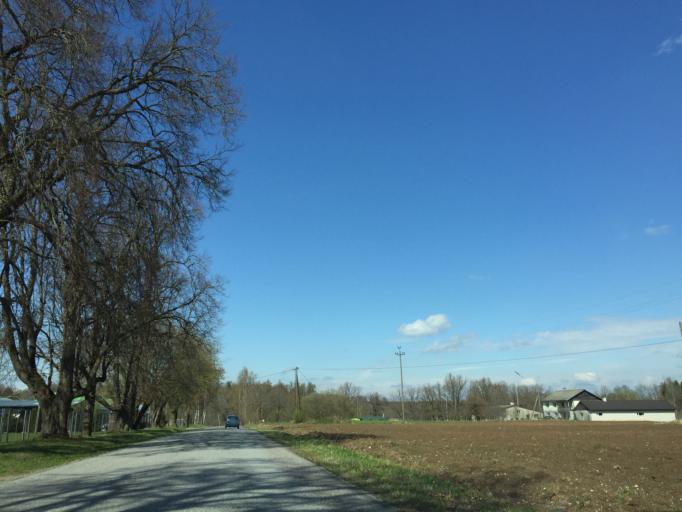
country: EE
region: Tartu
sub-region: Elva linn
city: Elva
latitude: 58.1489
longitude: 26.2329
